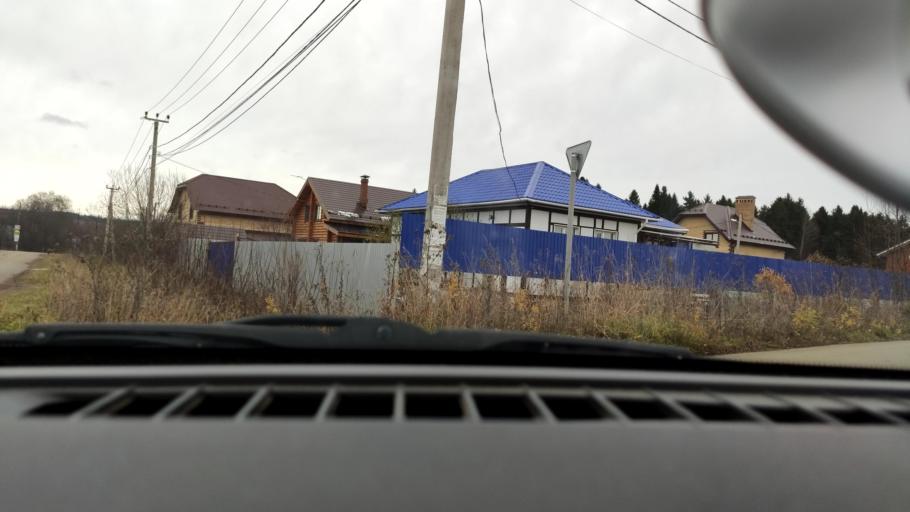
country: RU
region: Perm
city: Ferma
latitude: 57.9184
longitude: 56.3371
